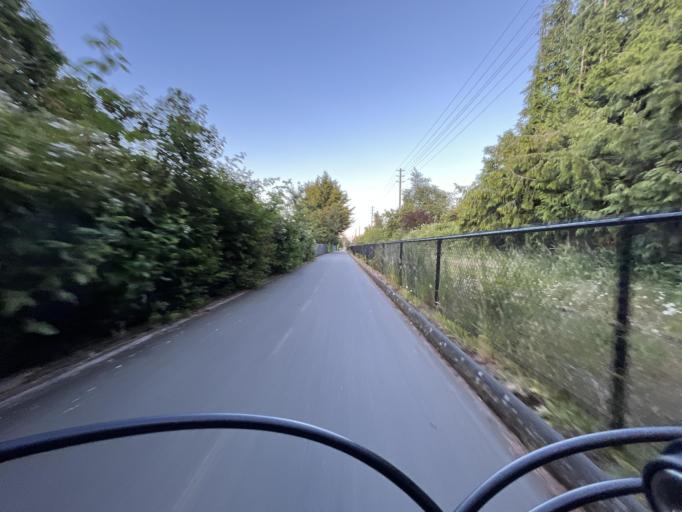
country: CA
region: British Columbia
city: Victoria
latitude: 48.4376
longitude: -123.4133
